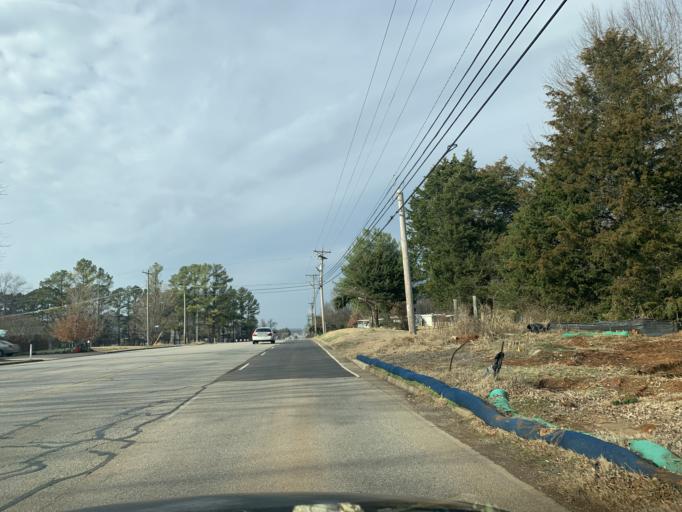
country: US
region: Tennessee
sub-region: Rutherford County
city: Smyrna
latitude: 35.9441
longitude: -86.5036
